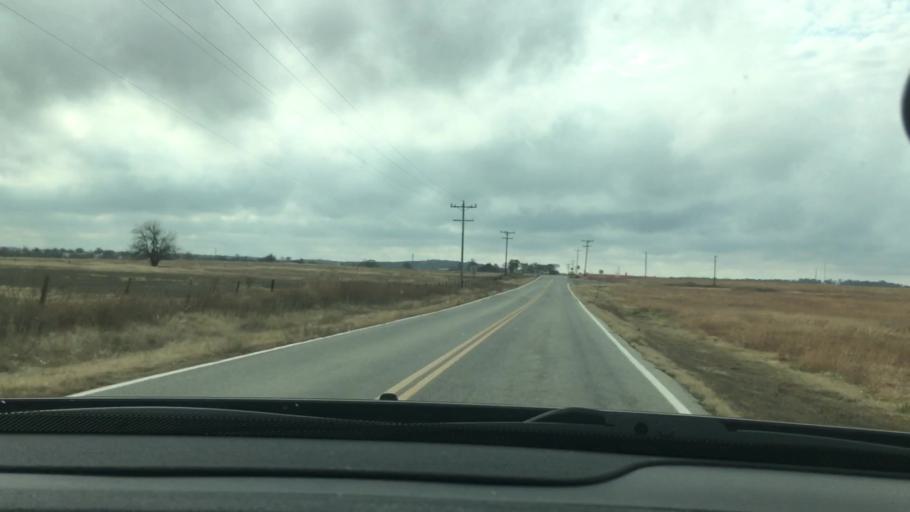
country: US
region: Oklahoma
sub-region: Bryan County
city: Durant
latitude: 34.1015
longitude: -96.4877
